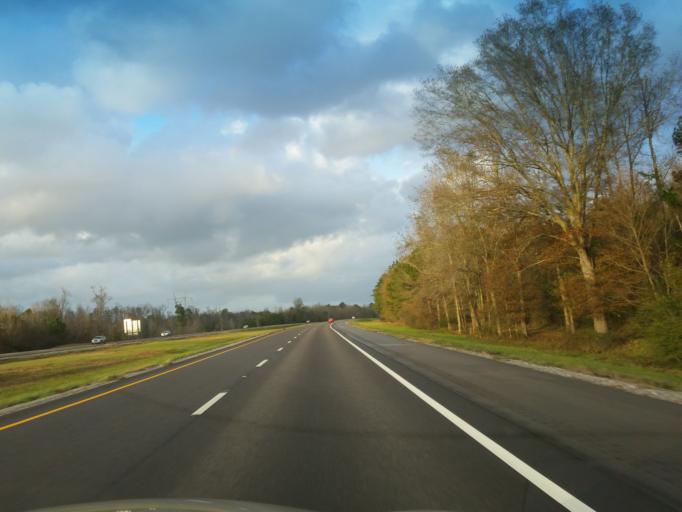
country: US
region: Mississippi
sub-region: Jones County
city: Sharon
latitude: 31.9196
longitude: -89.0047
